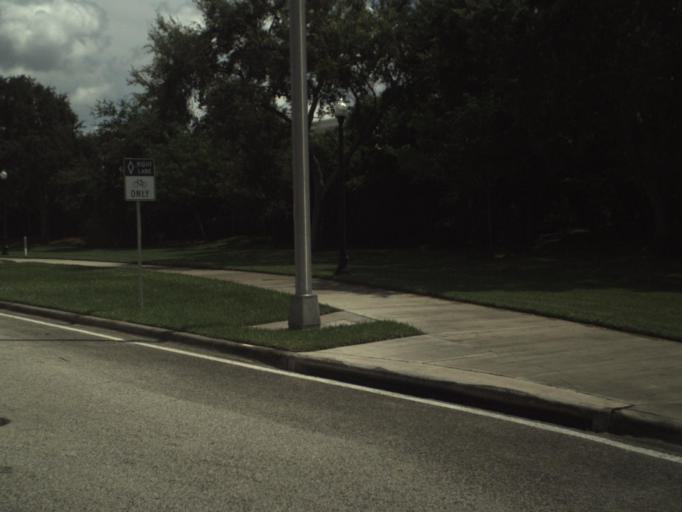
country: US
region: Florida
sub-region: Palm Beach County
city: North Palm Beach
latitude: 26.8400
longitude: -80.0940
